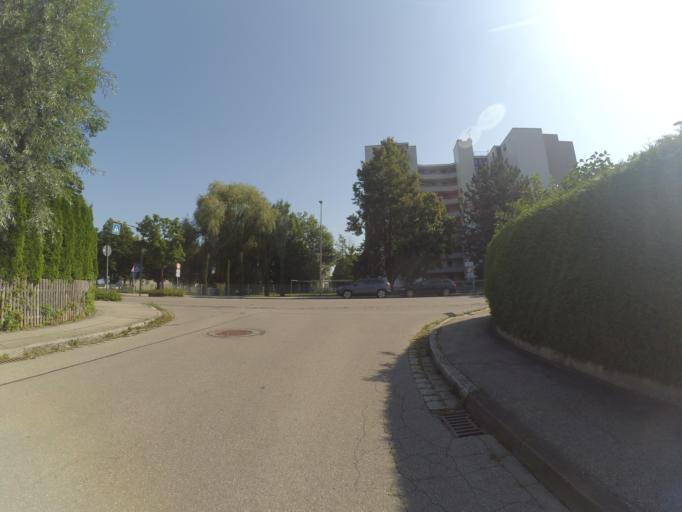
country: DE
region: Bavaria
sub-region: Swabia
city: Buchloe
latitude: 48.0307
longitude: 10.7246
